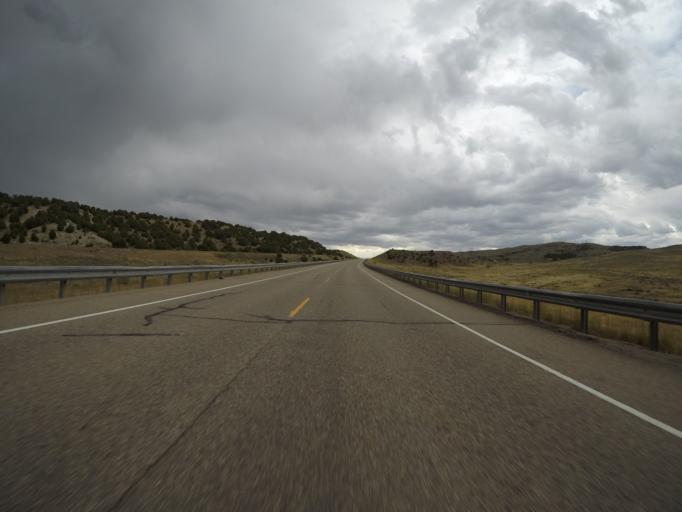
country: US
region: Colorado
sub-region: Rio Blanco County
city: Rangely
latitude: 40.3677
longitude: -108.4065
